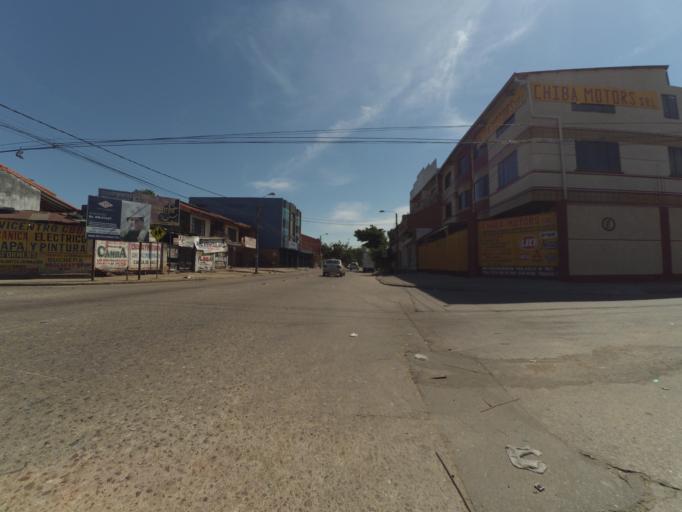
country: BO
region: Santa Cruz
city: Santa Cruz de la Sierra
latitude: -17.8062
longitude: -63.1969
